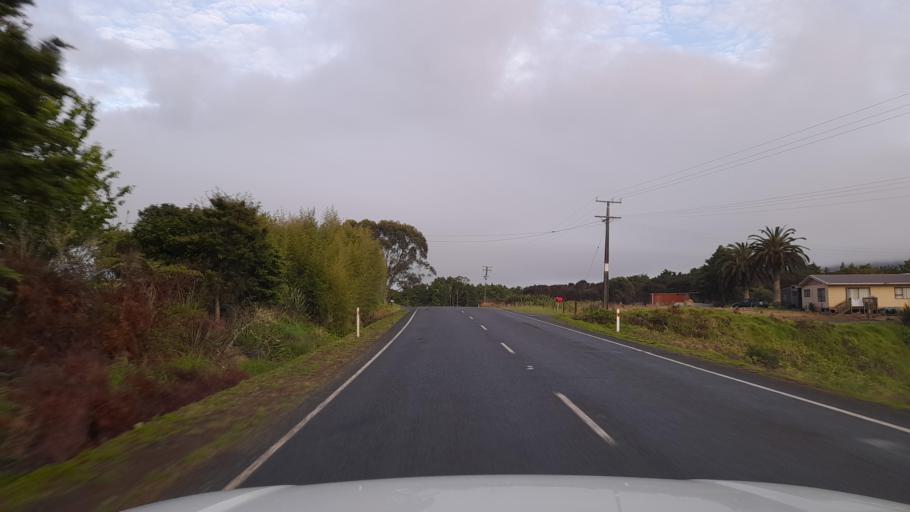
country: NZ
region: Northland
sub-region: Kaipara District
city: Dargaville
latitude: -35.7115
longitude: 173.9430
